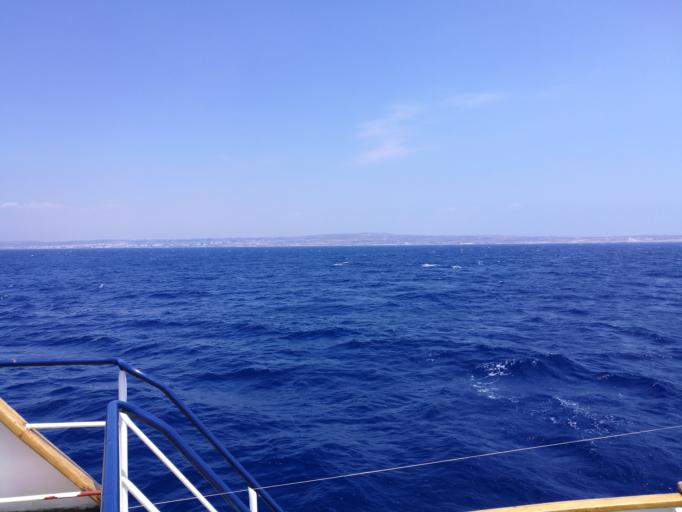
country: CY
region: Ammochostos
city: Ayia Napa
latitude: 34.9301
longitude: 34.0248
